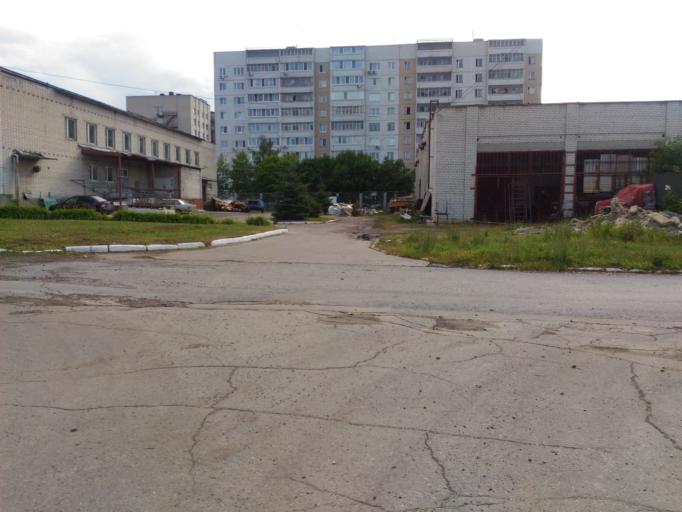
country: RU
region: Ulyanovsk
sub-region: Ulyanovskiy Rayon
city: Ulyanovsk
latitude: 54.3532
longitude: 48.3855
